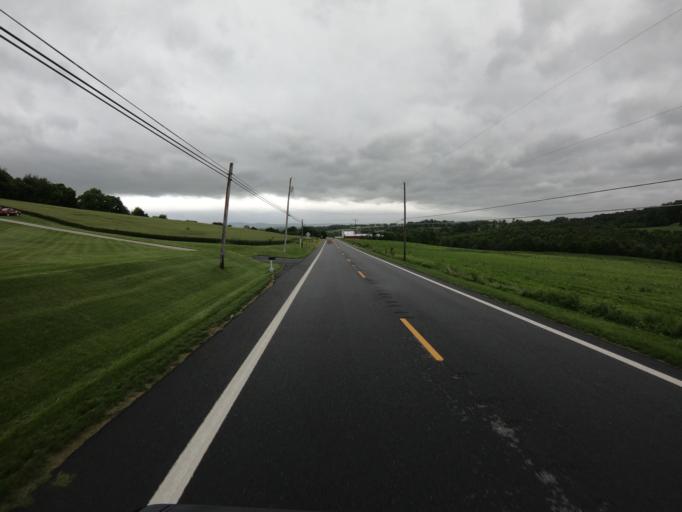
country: US
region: Maryland
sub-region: Frederick County
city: Myersville
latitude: 39.4749
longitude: -77.6054
